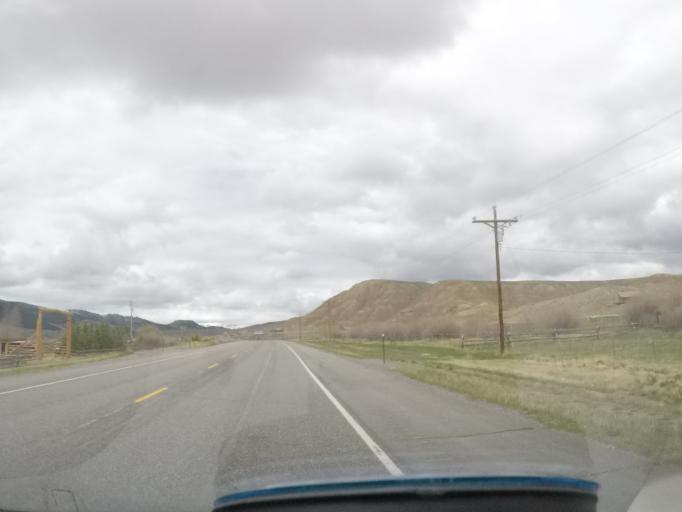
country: US
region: Wyoming
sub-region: Sublette County
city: Pinedale
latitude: 43.5664
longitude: -109.7065
